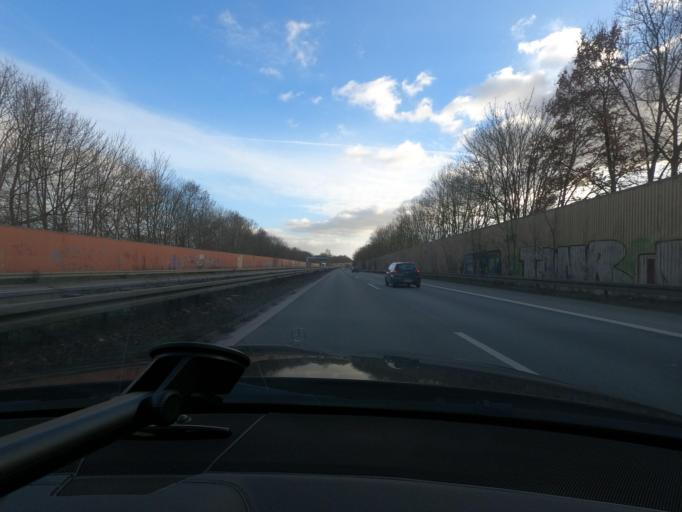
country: DE
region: North Rhine-Westphalia
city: Lunen
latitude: 51.5604
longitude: 7.5094
